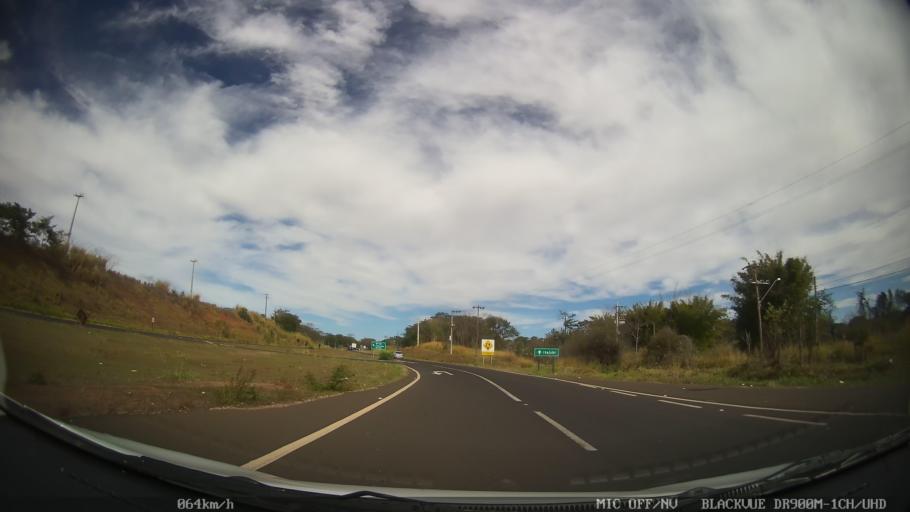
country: BR
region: Sao Paulo
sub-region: Catanduva
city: Catanduva
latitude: -21.1652
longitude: -48.9884
